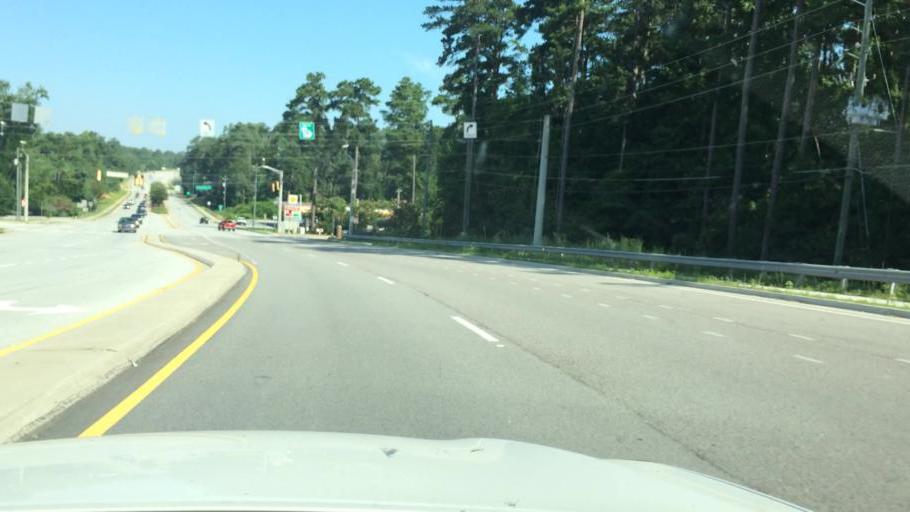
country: US
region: Georgia
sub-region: Columbia County
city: Martinez
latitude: 33.5192
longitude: -82.0617
